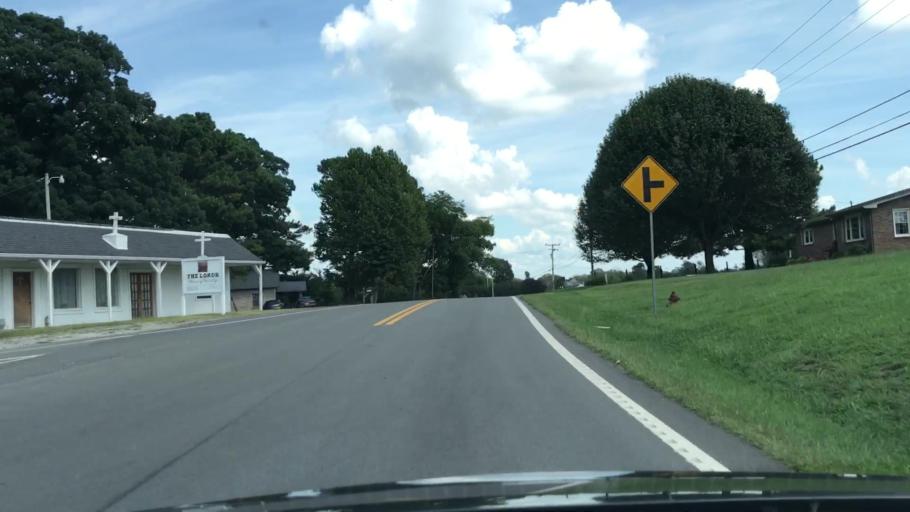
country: US
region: Tennessee
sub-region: Sumner County
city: Portland
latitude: 36.5359
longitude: -86.5293
